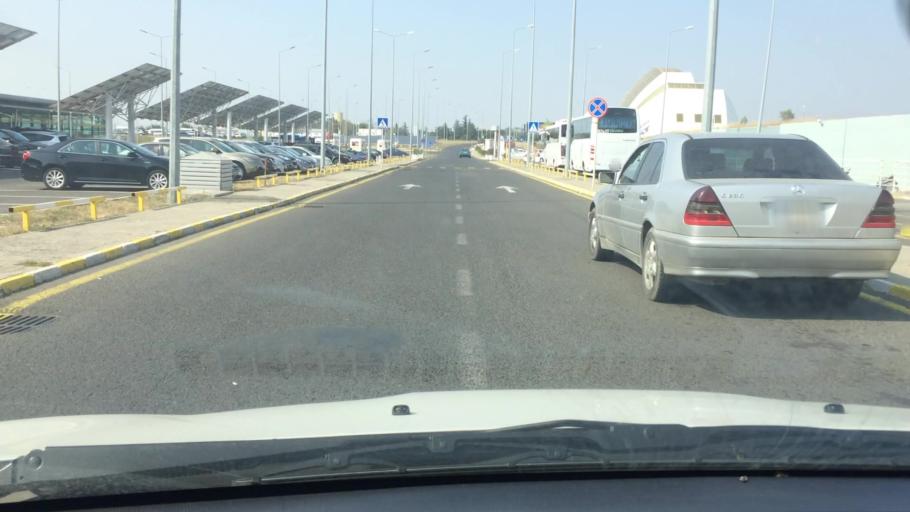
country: GE
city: Didi Lilo
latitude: 41.6701
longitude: 44.9658
